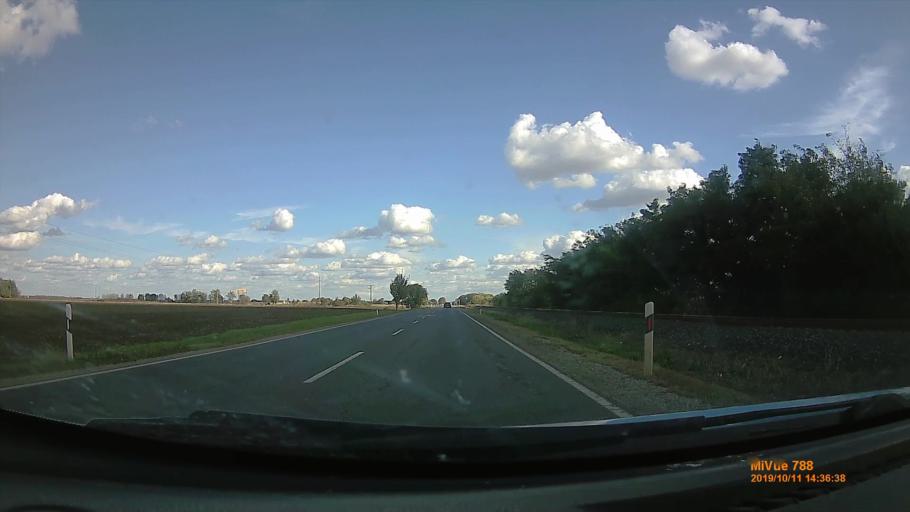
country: HU
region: Hajdu-Bihar
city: Ebes
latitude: 47.5564
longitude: 21.5118
